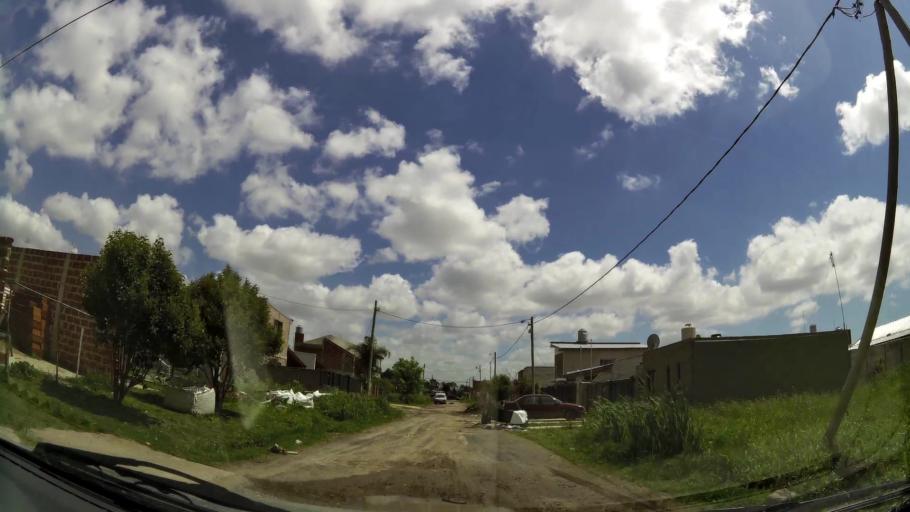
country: AR
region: Buenos Aires
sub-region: Partido de Quilmes
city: Quilmes
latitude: -34.8332
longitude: -58.2393
